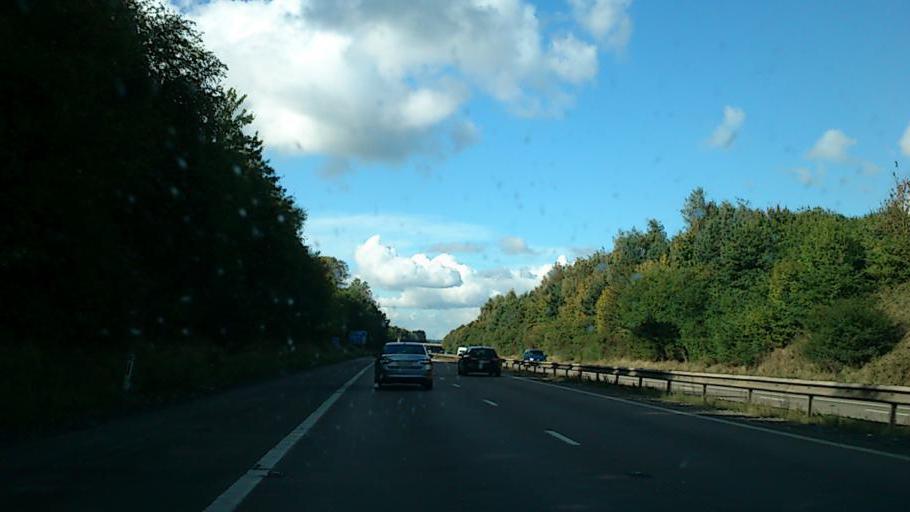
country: GB
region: England
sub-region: Shropshire
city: Albrighton
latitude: 52.6522
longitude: -2.2653
